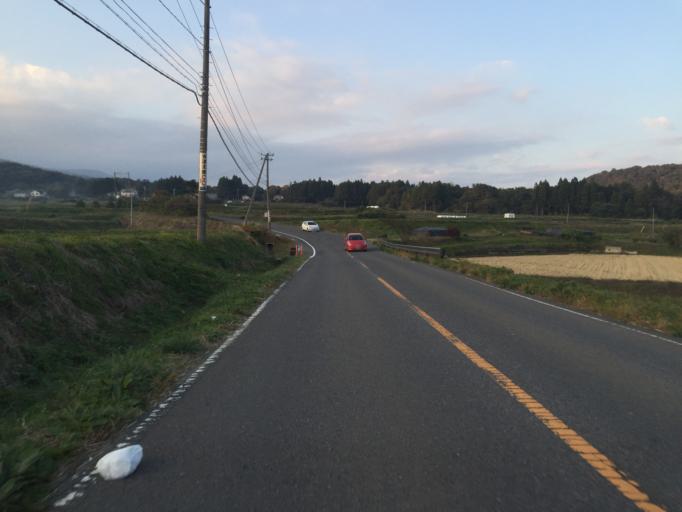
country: JP
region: Fukushima
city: Motomiya
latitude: 37.5652
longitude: 140.3516
